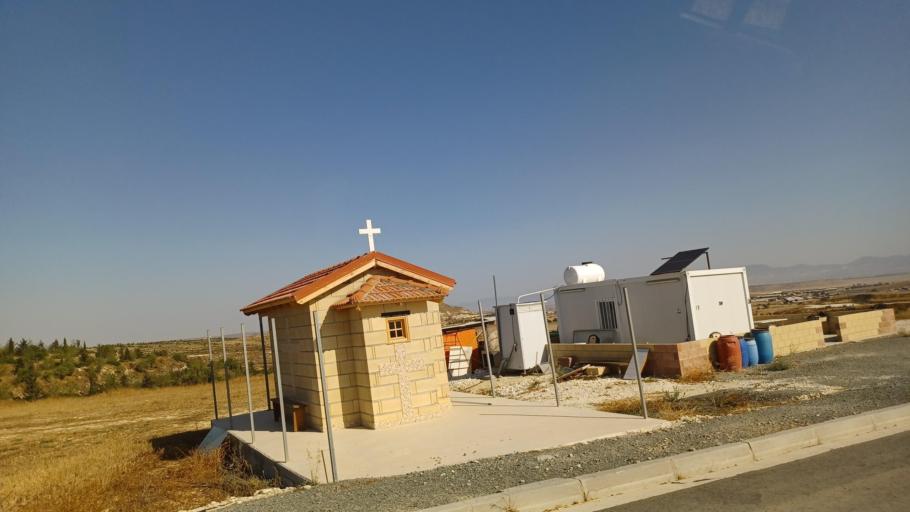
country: CY
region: Larnaka
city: Athienou
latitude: 35.0246
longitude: 33.5472
